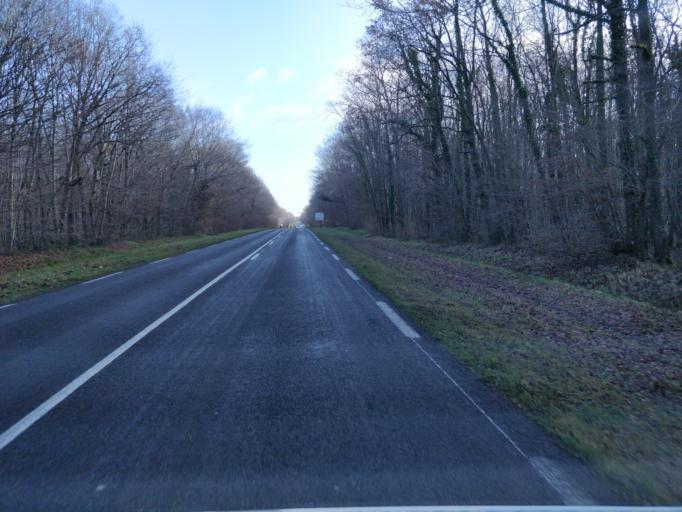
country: FR
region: Ile-de-France
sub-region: Departement de Seine-et-Marne
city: Souppes-sur-Loing
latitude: 48.2418
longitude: 2.8047
